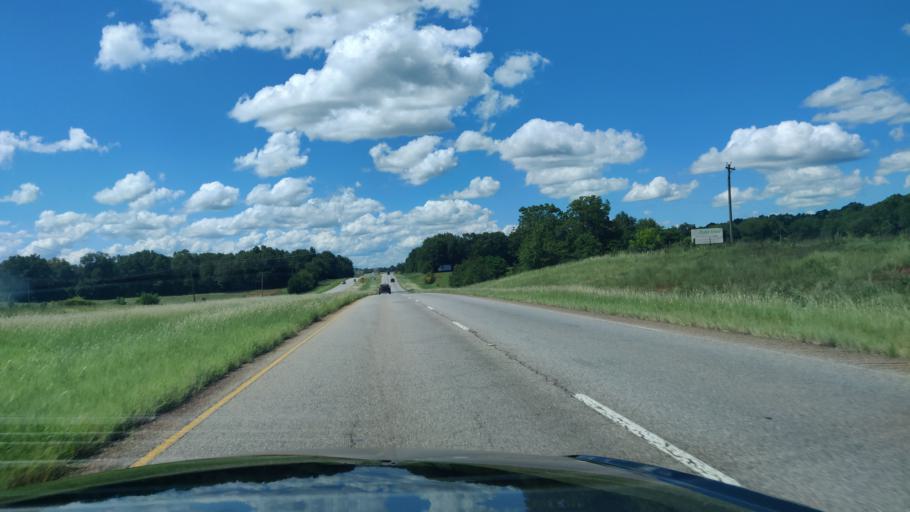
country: US
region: Georgia
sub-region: Stewart County
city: Richland
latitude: 32.0793
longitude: -84.6739
